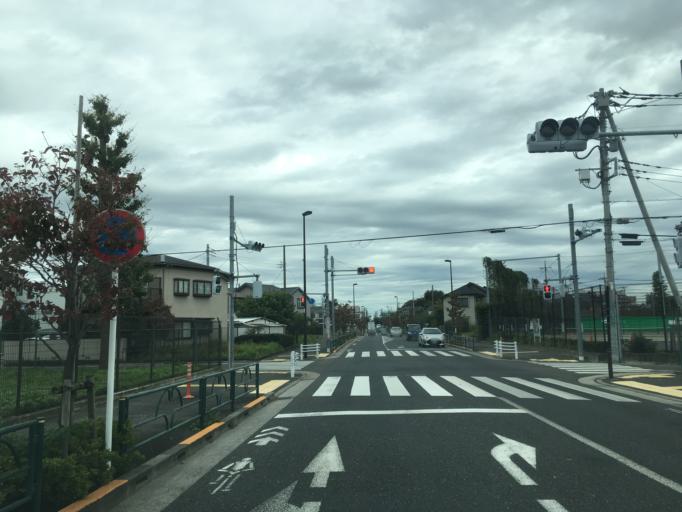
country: JP
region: Tokyo
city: Chofugaoka
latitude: 35.6299
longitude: 139.5712
